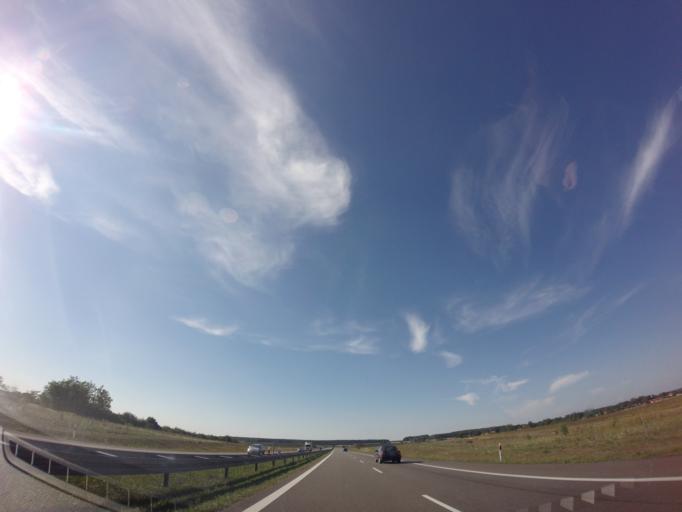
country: PL
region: Lubusz
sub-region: Powiat zielonogorski
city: Sulechow
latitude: 52.1154
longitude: 15.5810
